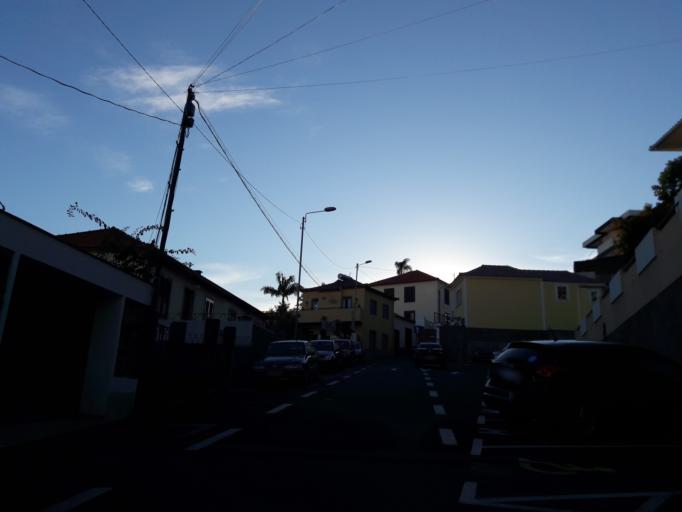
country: PT
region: Madeira
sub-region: Funchal
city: Nossa Senhora do Monte
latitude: 32.6558
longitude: -16.9065
